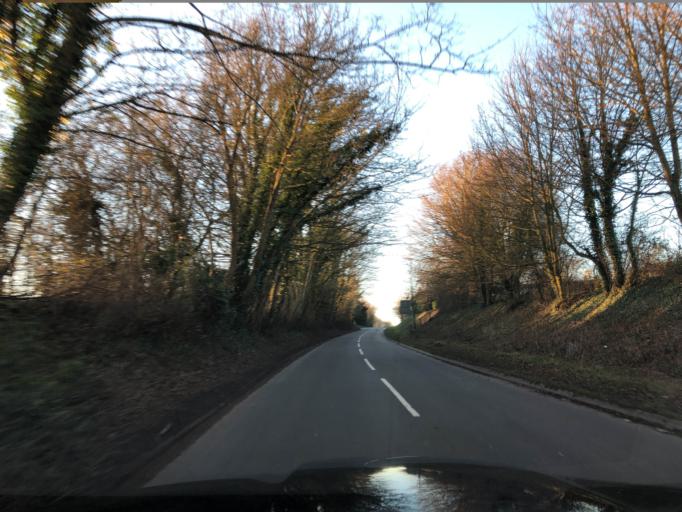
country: GB
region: England
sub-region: Warwickshire
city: Harbury
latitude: 52.2154
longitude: -1.4364
